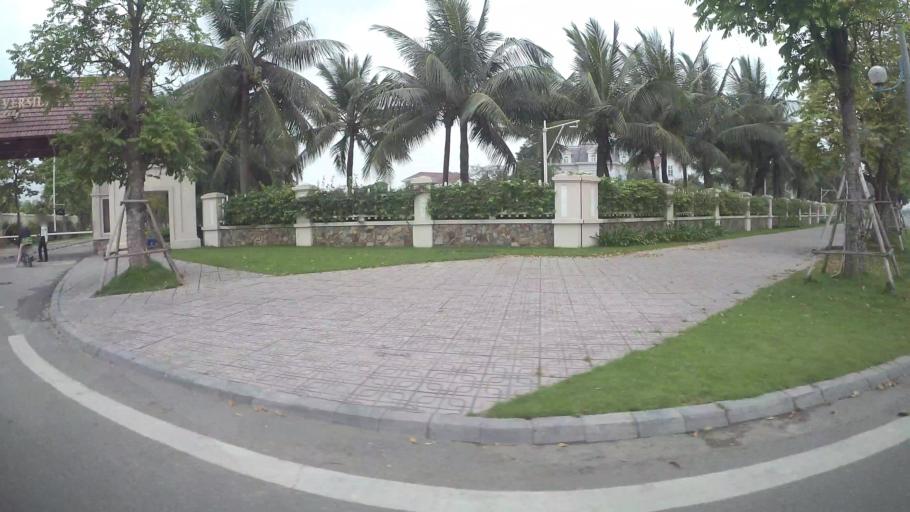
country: VN
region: Ha Noi
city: Trau Quy
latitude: 21.0484
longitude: 105.9124
